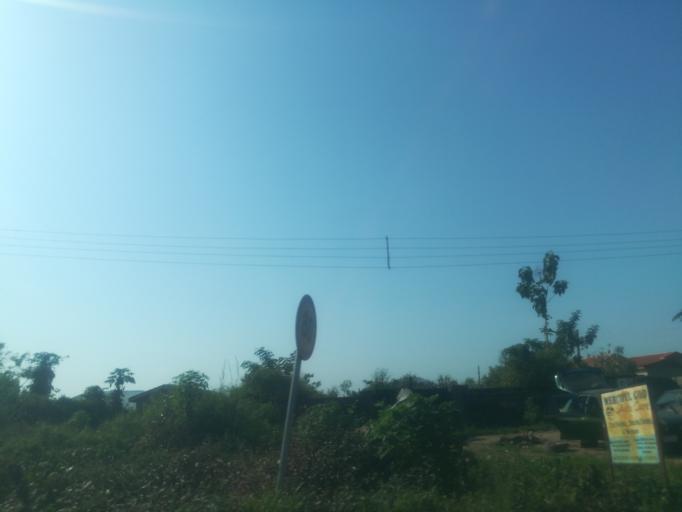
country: NG
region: Ogun
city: Abeokuta
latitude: 7.1648
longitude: 3.2687
